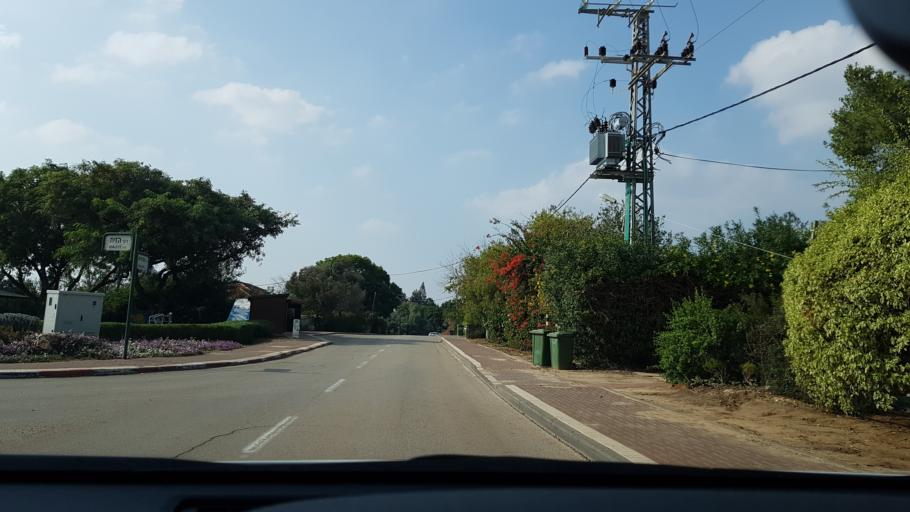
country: IL
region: Central District
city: Mazkeret Batya
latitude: 31.8703
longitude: 34.8265
